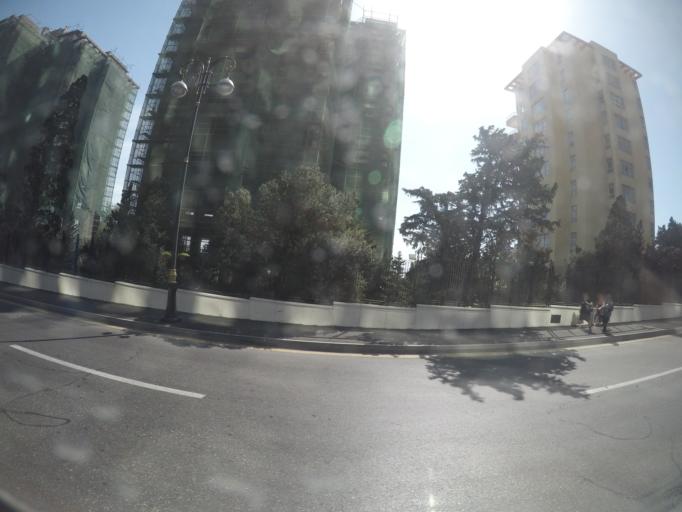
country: AZ
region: Baki
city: Badamdar
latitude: 40.3607
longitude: 49.8269
